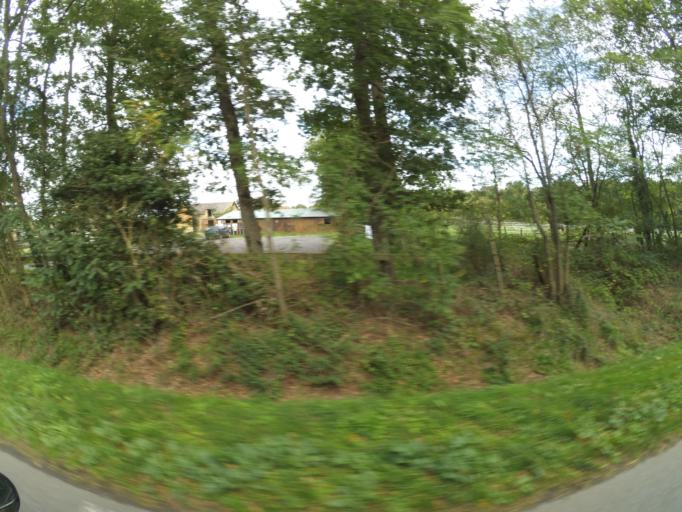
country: FR
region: Pays de la Loire
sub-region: Departement de la Loire-Atlantique
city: Plesse
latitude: 47.5056
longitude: -1.8736
